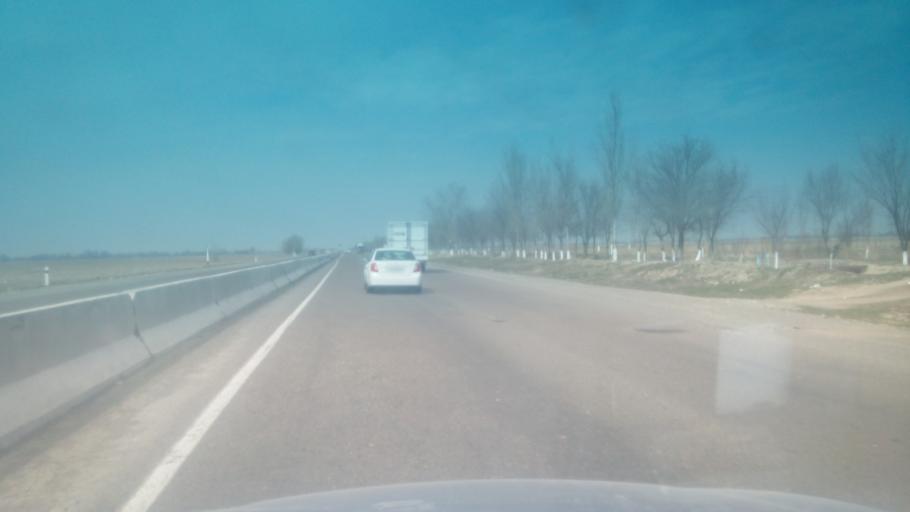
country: KZ
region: Ongtustik Qazaqstan
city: Myrzakent
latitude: 40.5261
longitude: 68.4470
